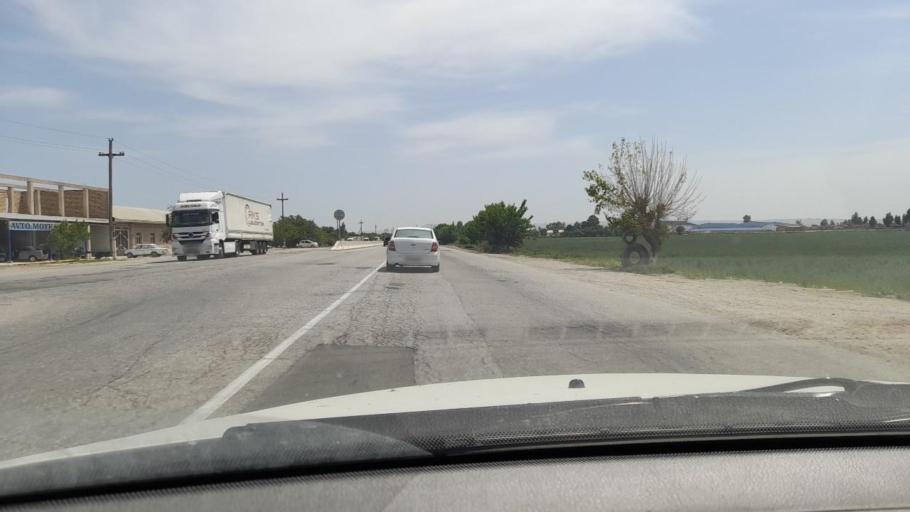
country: UZ
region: Navoiy
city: Karmana Shahri
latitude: 40.1359
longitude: 65.4036
